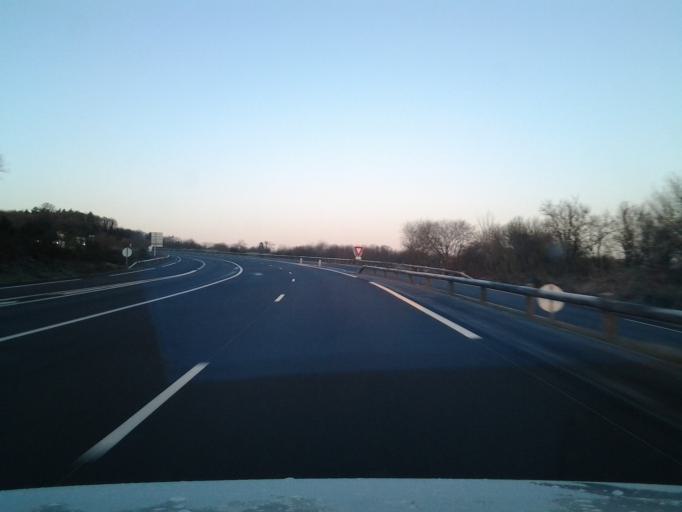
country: FR
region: Pays de la Loire
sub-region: Departement de la Vendee
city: Chambretaud
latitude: 46.9180
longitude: -0.9602
